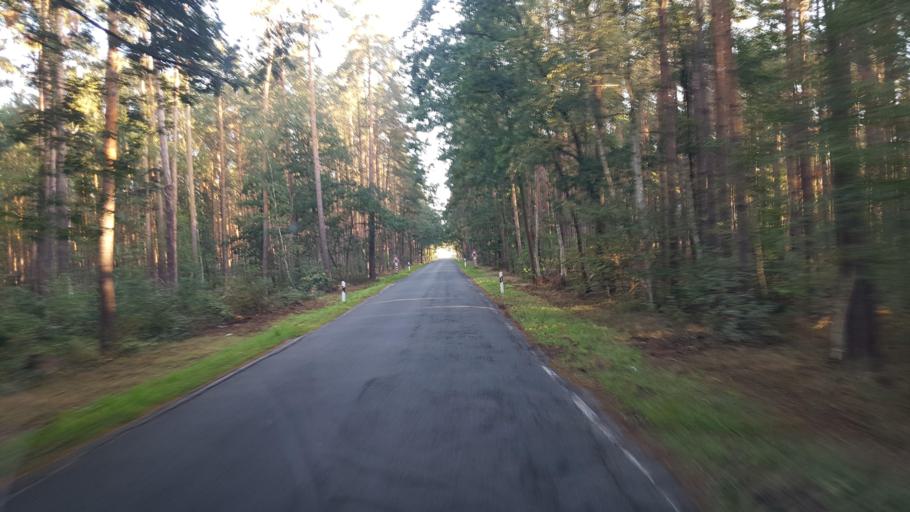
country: DE
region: Saxony-Anhalt
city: Holzdorf
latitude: 51.8400
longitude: 13.0879
